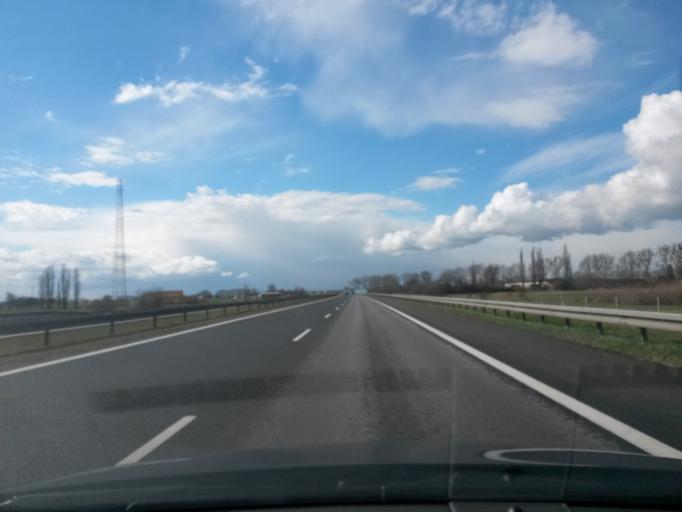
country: PL
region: Greater Poland Voivodeship
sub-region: Powiat wrzesinski
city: Kolaczkowo
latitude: 52.2885
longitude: 17.6733
